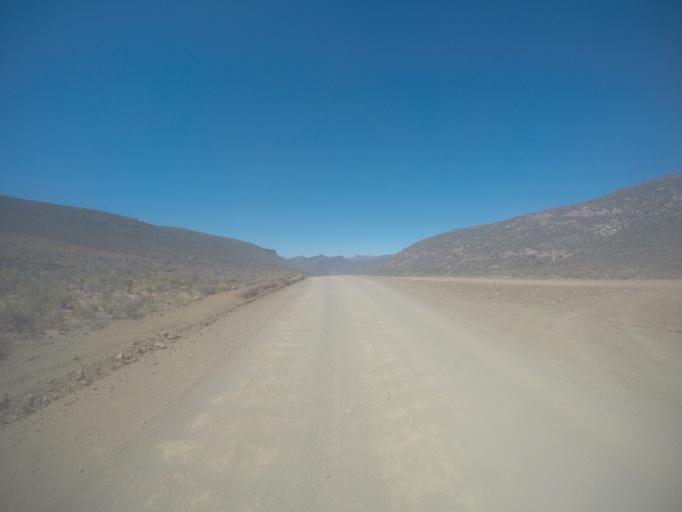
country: ZA
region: Western Cape
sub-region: West Coast District Municipality
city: Clanwilliam
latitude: -32.5300
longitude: 19.3540
